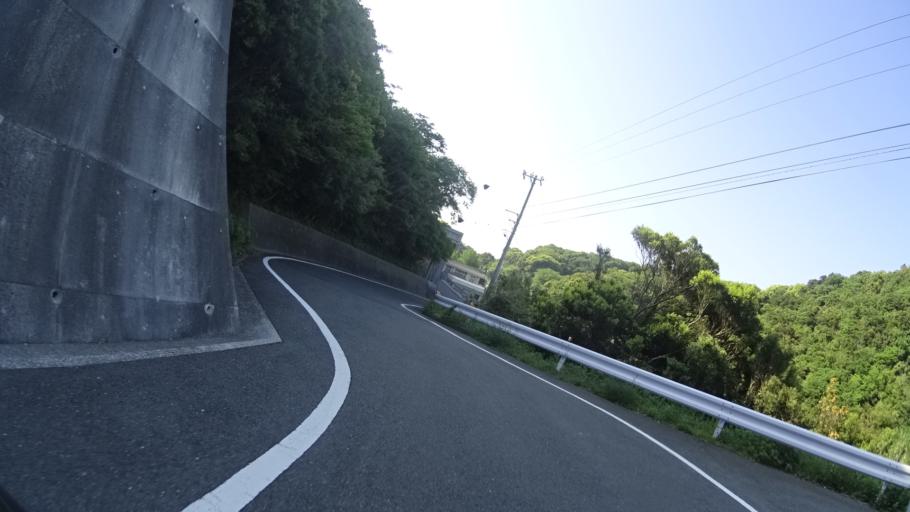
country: JP
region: Oita
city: Tsukumiura
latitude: 33.3556
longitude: 132.0384
